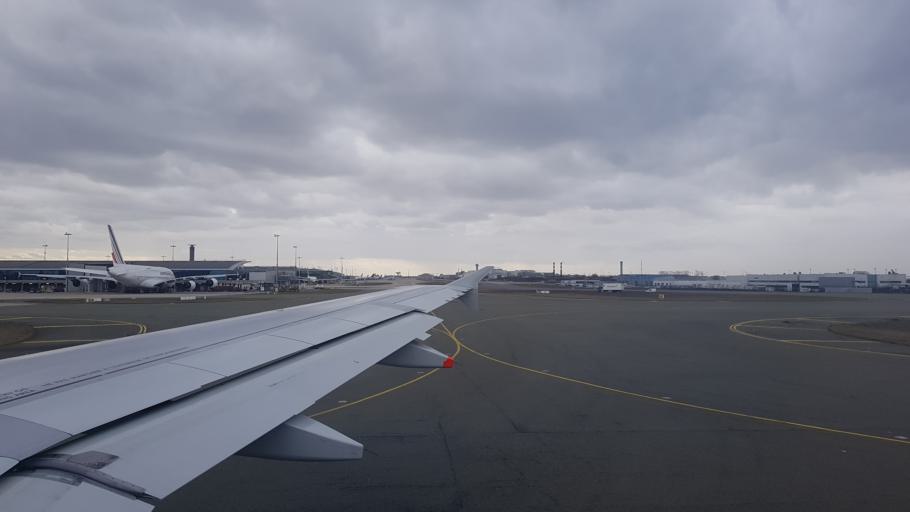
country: FR
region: Ile-de-France
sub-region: Departement de Seine-et-Marne
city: Mitry-Mory
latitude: 49.0090
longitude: 2.5954
